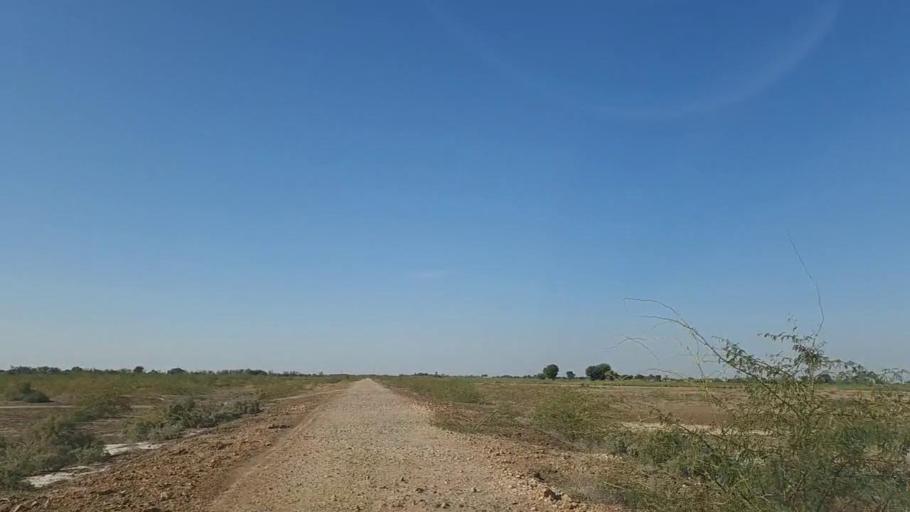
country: PK
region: Sindh
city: Kunri
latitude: 25.2442
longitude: 69.4971
